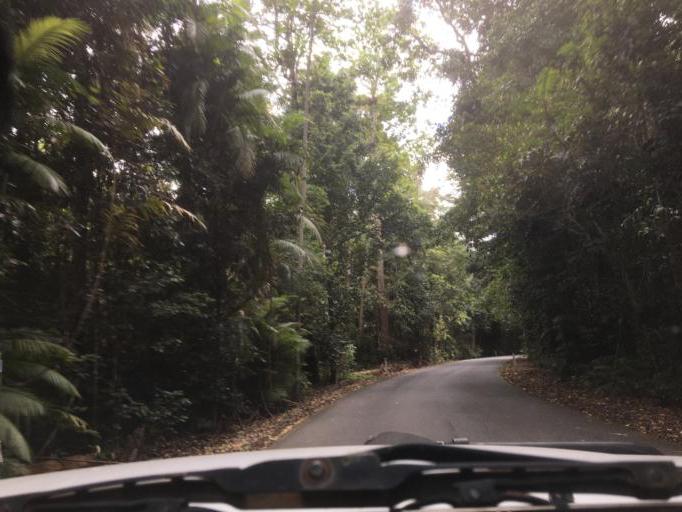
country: AU
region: Queensland
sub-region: Tablelands
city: Atherton
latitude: -17.2832
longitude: 145.6183
